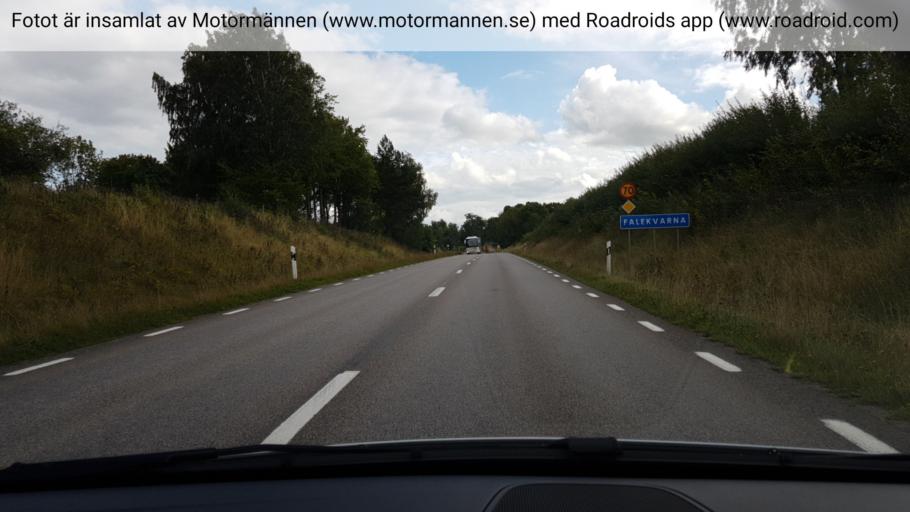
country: SE
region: Vaestra Goetaland
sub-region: Falkopings Kommun
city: Akarp
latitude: 58.1299
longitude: 13.6581
